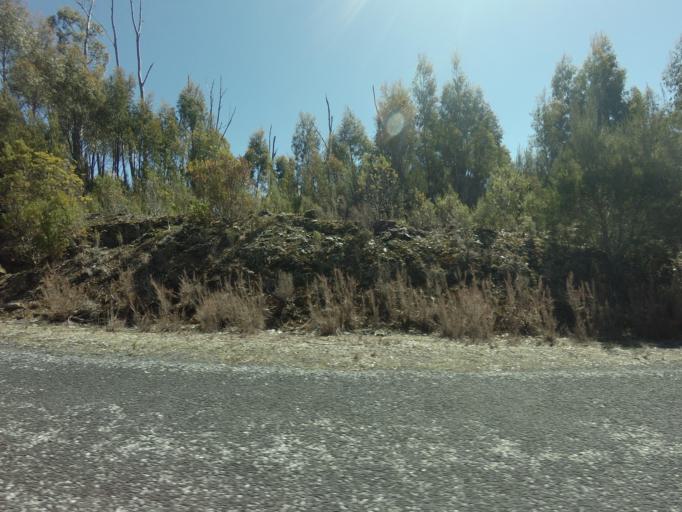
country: AU
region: Tasmania
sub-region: Huon Valley
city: Geeveston
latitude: -42.8096
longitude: 146.0967
